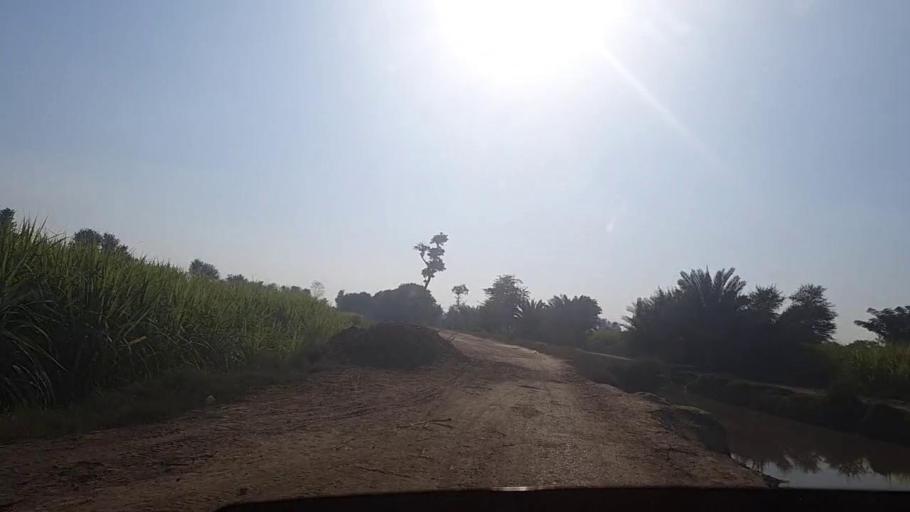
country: PK
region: Sindh
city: Gambat
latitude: 27.3778
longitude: 68.4680
